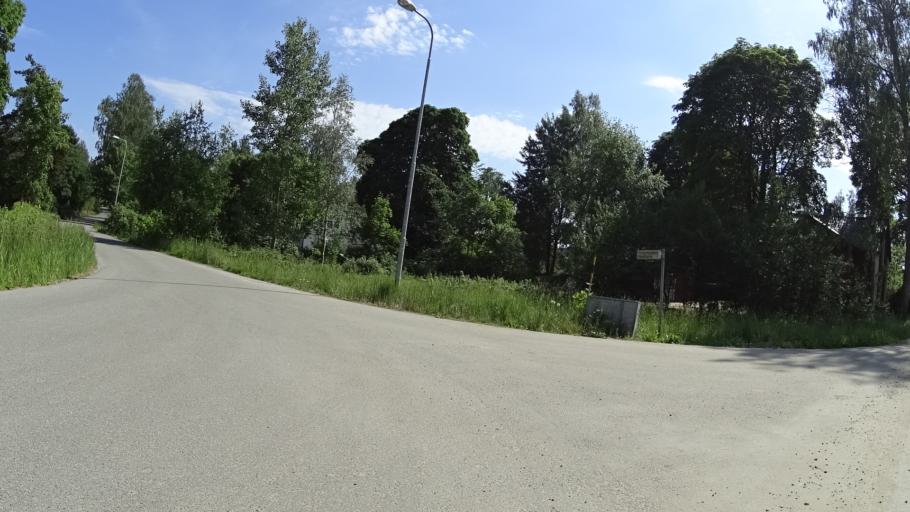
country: FI
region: Uusimaa
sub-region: Raaseporin
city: Karis
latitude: 60.0873
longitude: 23.6496
